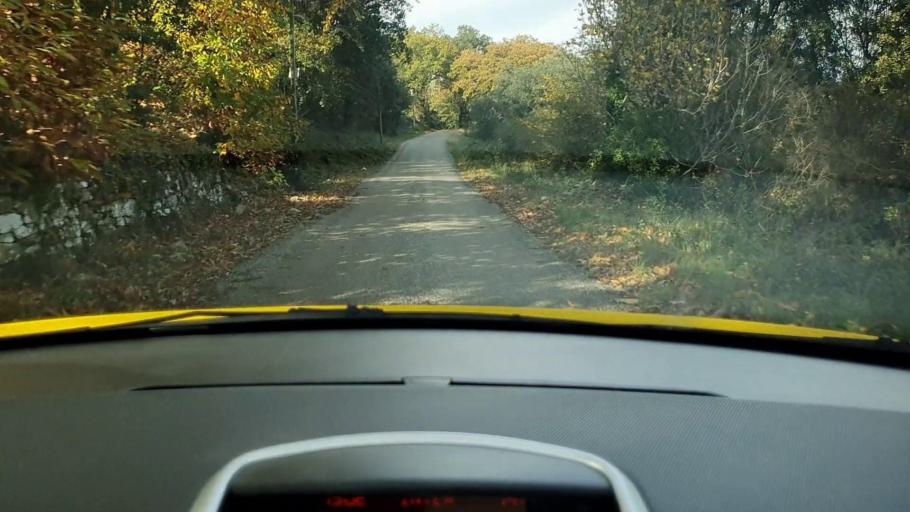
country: FR
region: Languedoc-Roussillon
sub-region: Departement du Gard
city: Anduze
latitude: 44.0355
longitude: 3.9272
